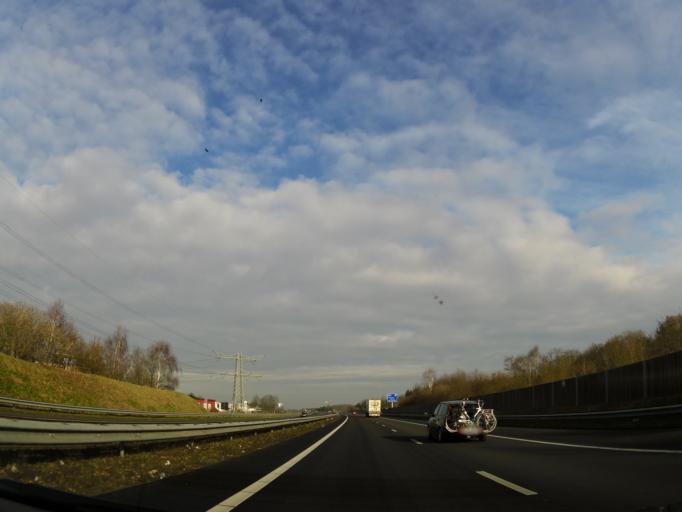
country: NL
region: Limburg
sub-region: Gemeente Venray
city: Venray
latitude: 51.5382
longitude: 5.9990
